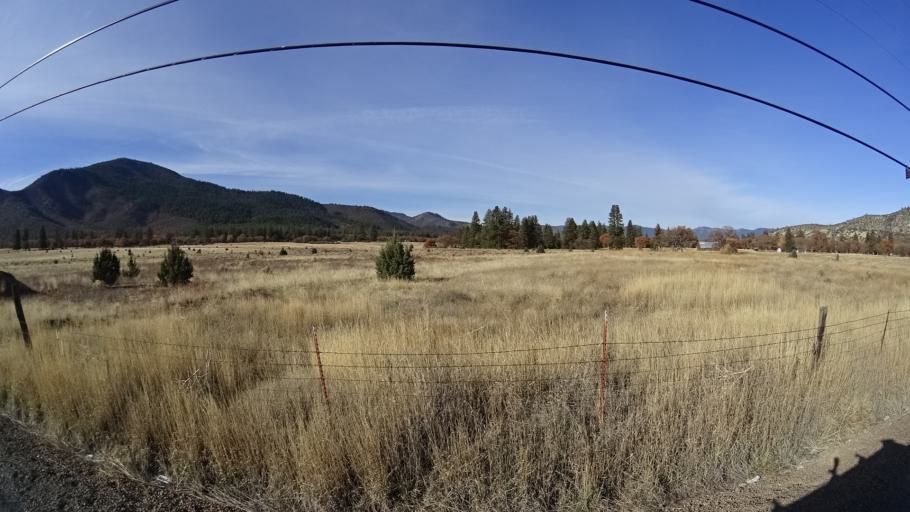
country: US
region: California
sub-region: Siskiyou County
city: Montague
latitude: 41.6551
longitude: -122.5829
